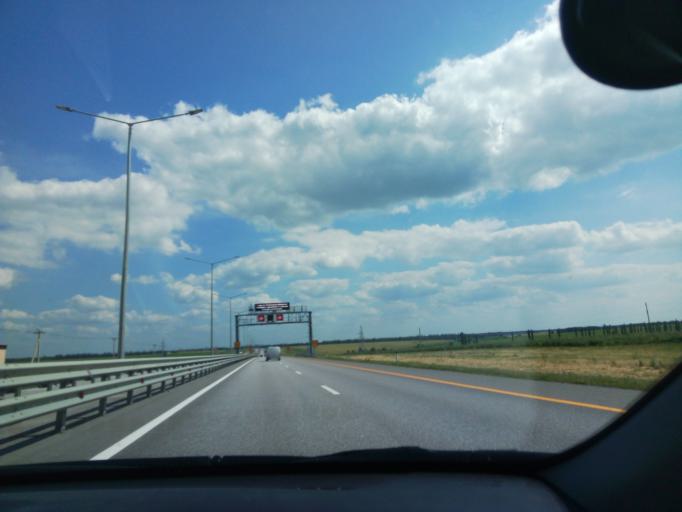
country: RU
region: Voronezj
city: Podkletnoye
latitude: 51.4973
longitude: 39.5247
